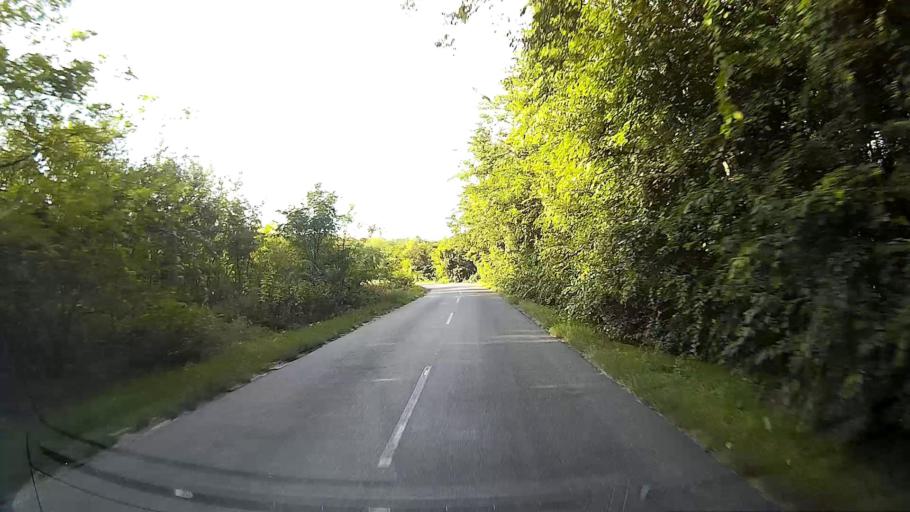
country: HU
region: Pest
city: Mogyorod
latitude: 47.5855
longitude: 19.2312
